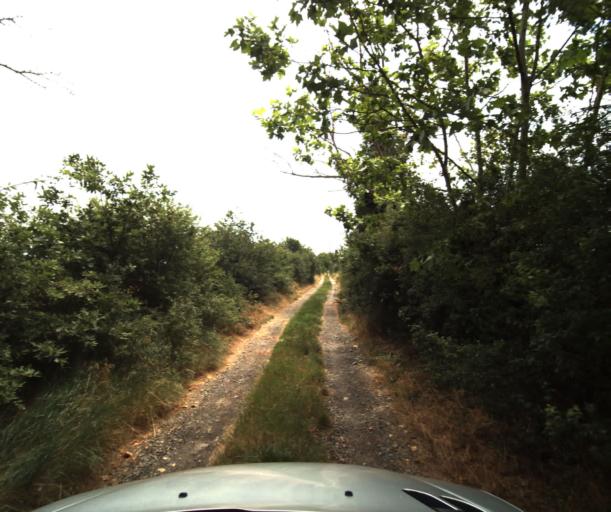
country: FR
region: Midi-Pyrenees
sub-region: Departement de la Haute-Garonne
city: Lacasse
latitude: 43.4125
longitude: 1.2665
